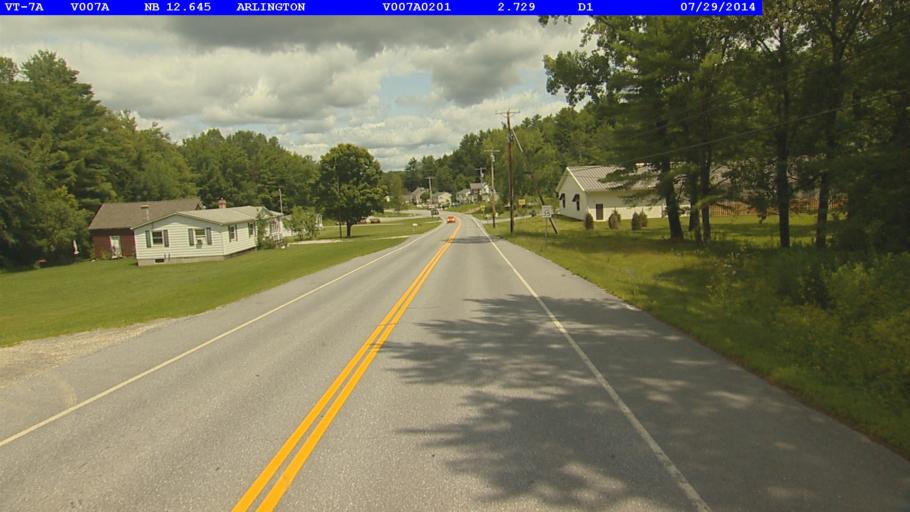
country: US
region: Vermont
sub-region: Bennington County
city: Arlington
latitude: 43.0589
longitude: -73.1606
